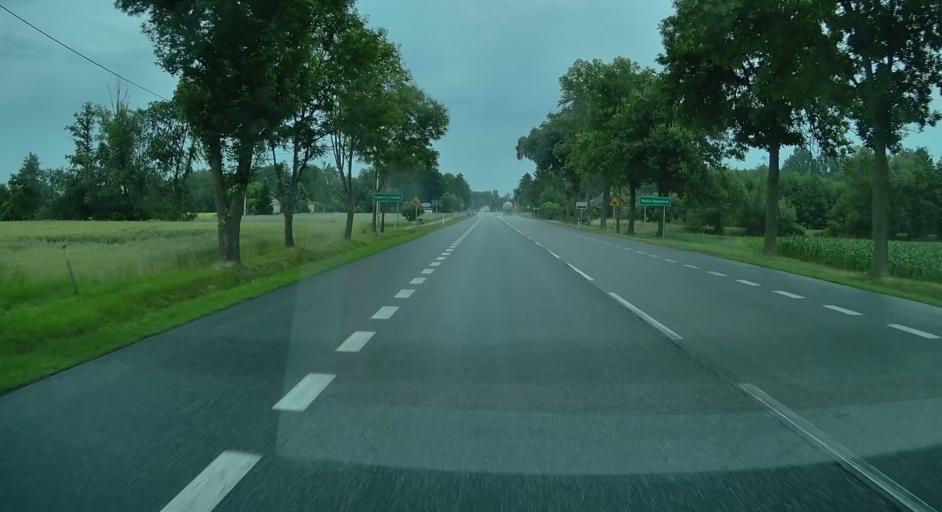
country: PL
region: Masovian Voivodeship
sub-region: Powiat siedlecki
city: Zbuczyn
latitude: 52.0700
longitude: 22.5160
